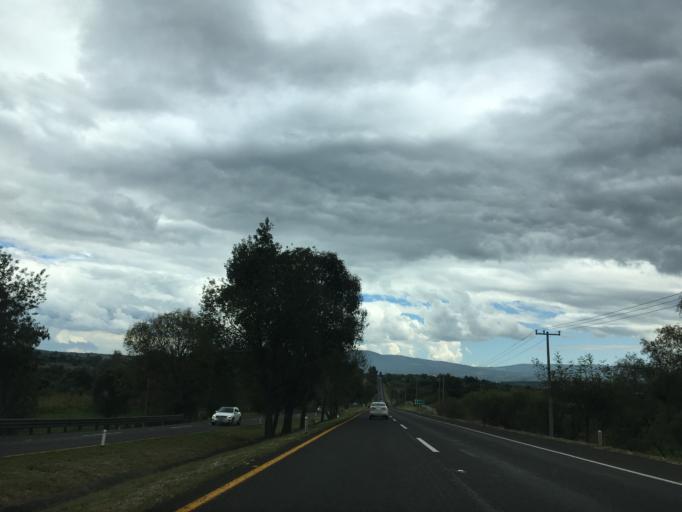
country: MX
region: Michoacan
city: Lagunillas
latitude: 19.5585
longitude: -101.3987
